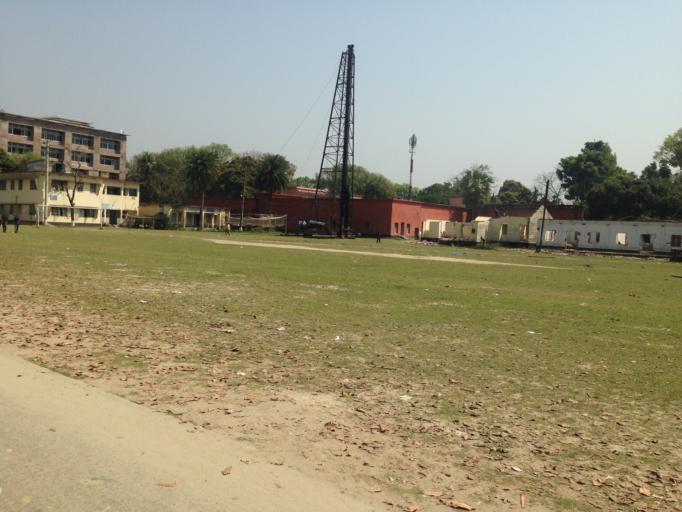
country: BD
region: Dhaka
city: Tangail
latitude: 24.2355
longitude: 89.8902
